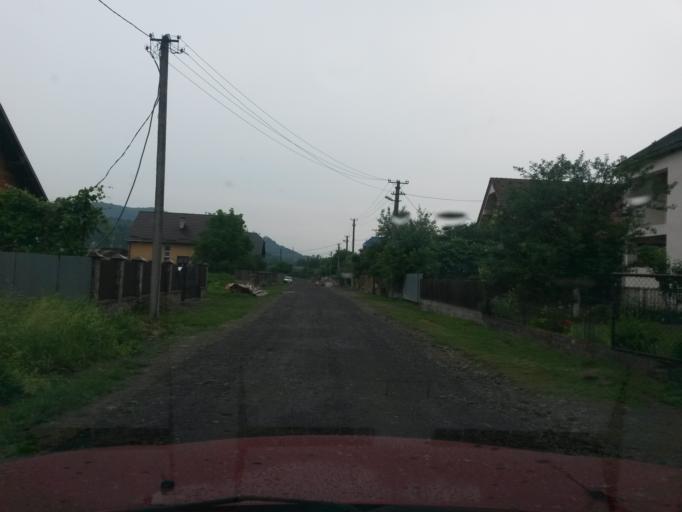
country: UA
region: Zakarpattia
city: Velykyi Bereznyi
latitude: 48.9052
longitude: 22.4651
